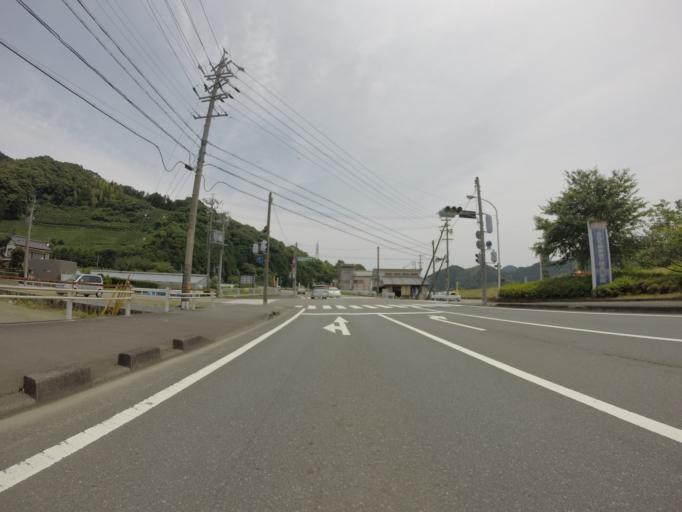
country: JP
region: Shizuoka
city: Shizuoka-shi
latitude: 34.9857
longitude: 138.3092
